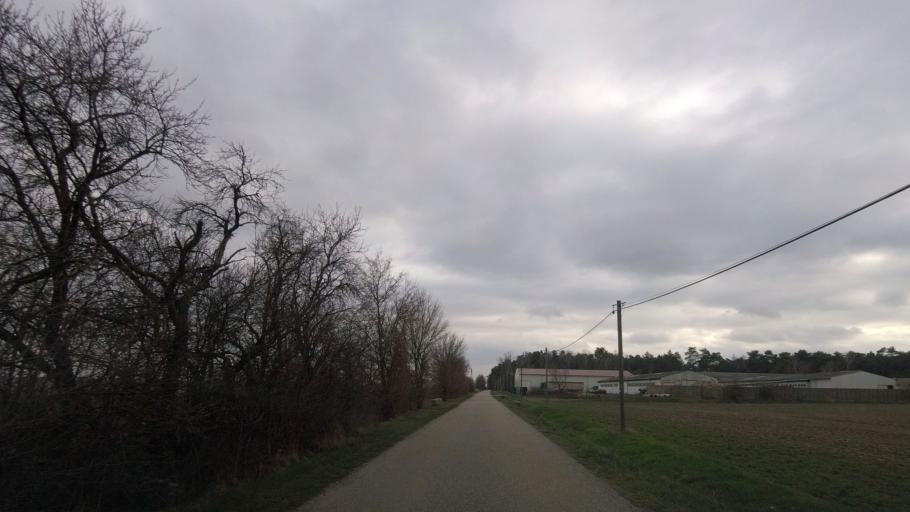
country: DE
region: Saxony-Anhalt
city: Seyda
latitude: 51.9207
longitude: 12.8880
